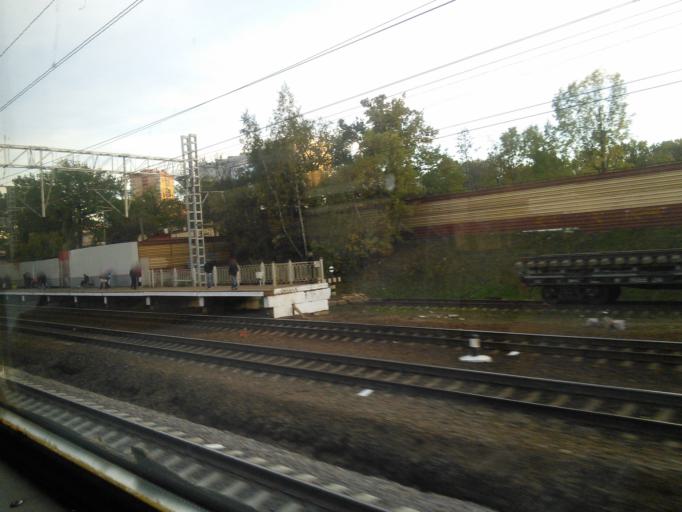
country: RU
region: Moscow
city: Khimki
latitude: 55.8958
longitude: 37.4482
